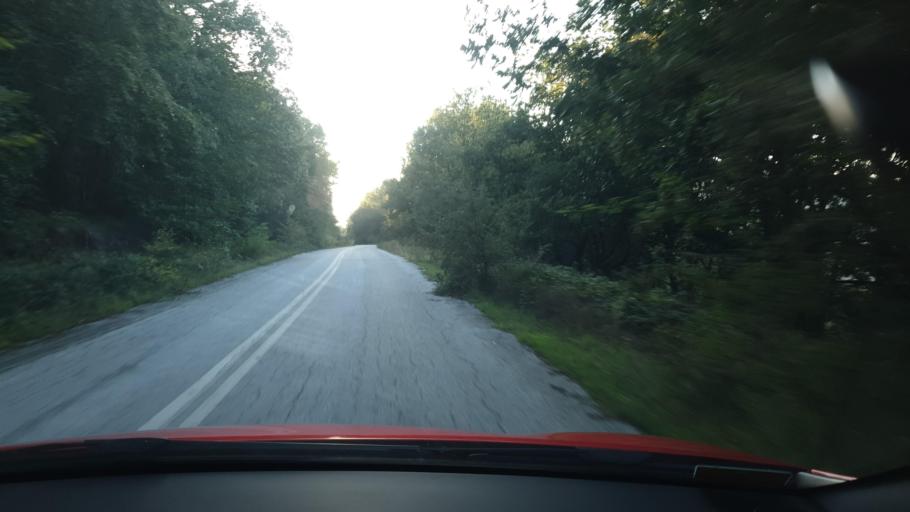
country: GR
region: Central Macedonia
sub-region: Nomos Chalkidikis
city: Galatista
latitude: 40.5071
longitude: 23.2465
